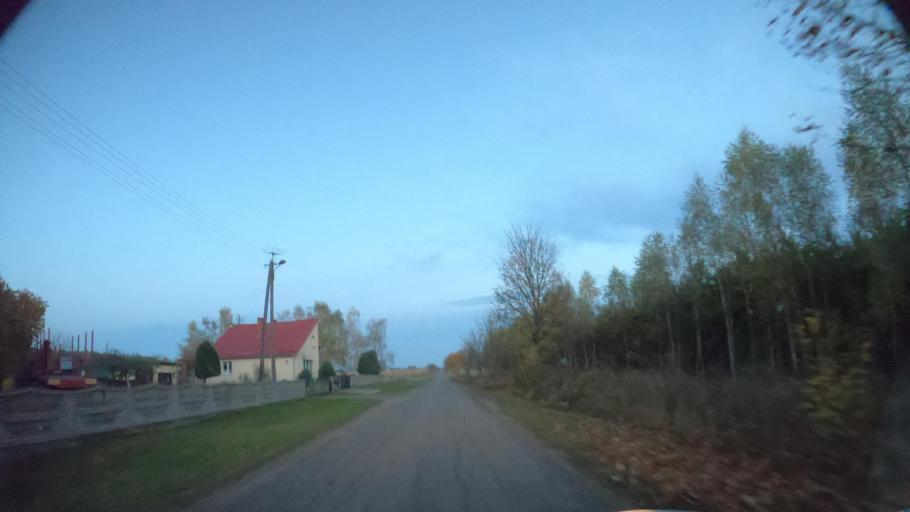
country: PL
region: Greater Poland Voivodeship
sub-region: Powiat zlotowski
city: Sypniewo
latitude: 53.4265
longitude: 16.6083
